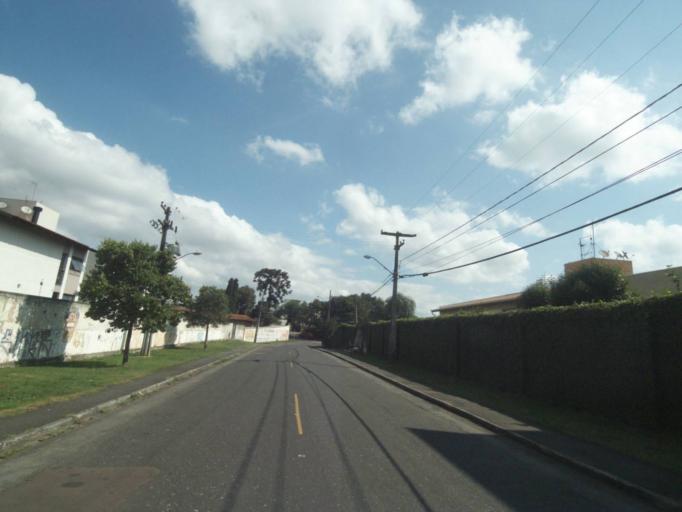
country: BR
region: Parana
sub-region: Curitiba
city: Curitiba
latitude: -25.4986
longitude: -49.3136
